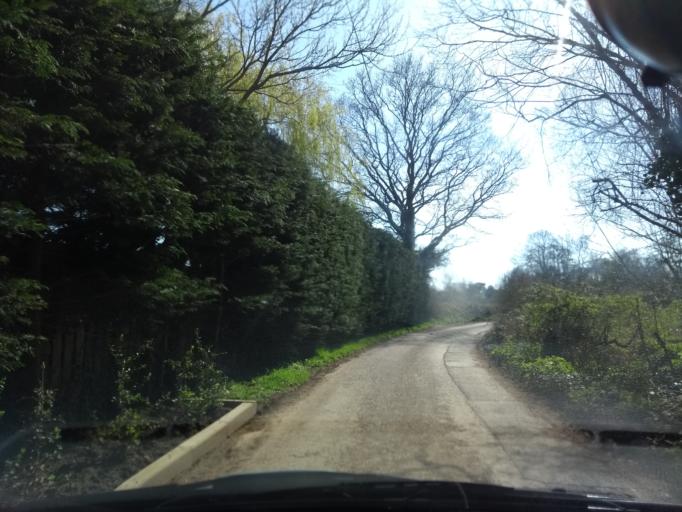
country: GB
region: England
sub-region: Somerset
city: Taunton
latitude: 51.0394
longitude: -3.1406
